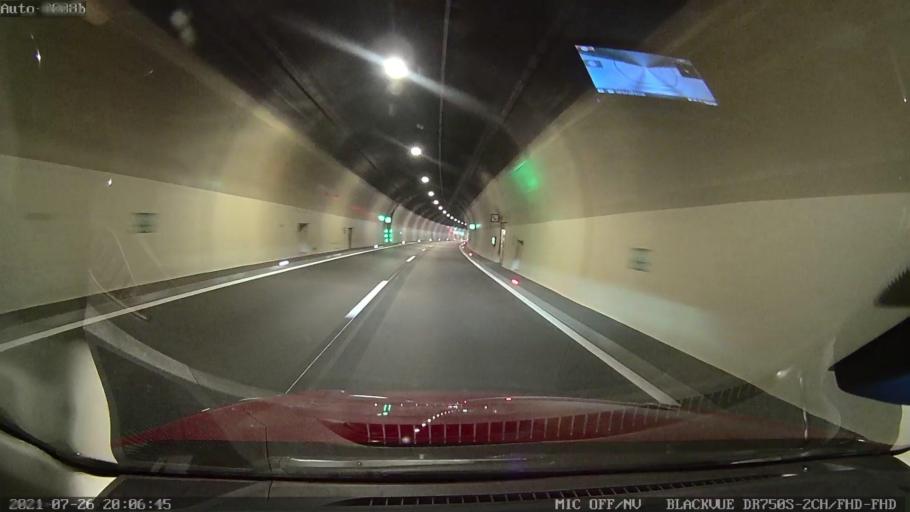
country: AT
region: Styria
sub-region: Politischer Bezirk Leoben
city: Wald am Schoberpass
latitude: 47.4440
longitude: 14.6846
